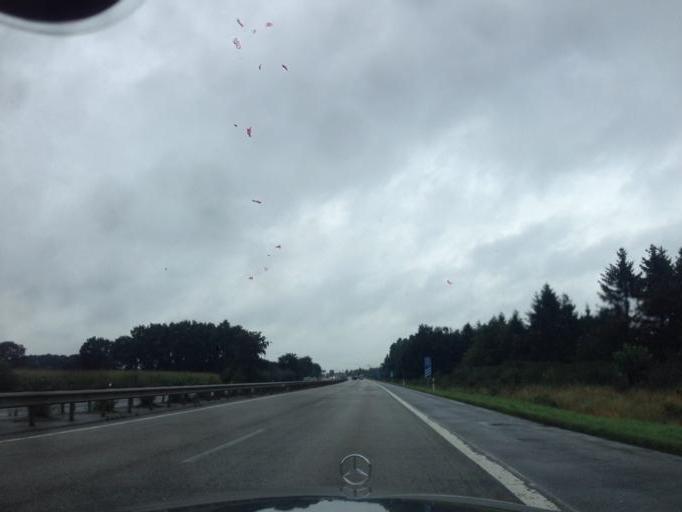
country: DE
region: Schleswig-Holstein
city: Padenstedt
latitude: 54.0368
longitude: 9.9321
